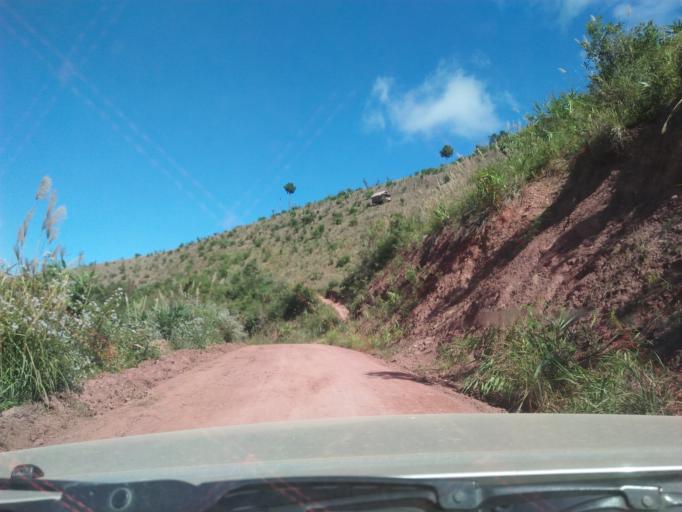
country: TH
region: Nan
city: Chaloem Phra Kiat
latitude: 19.4430
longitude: 101.2745
